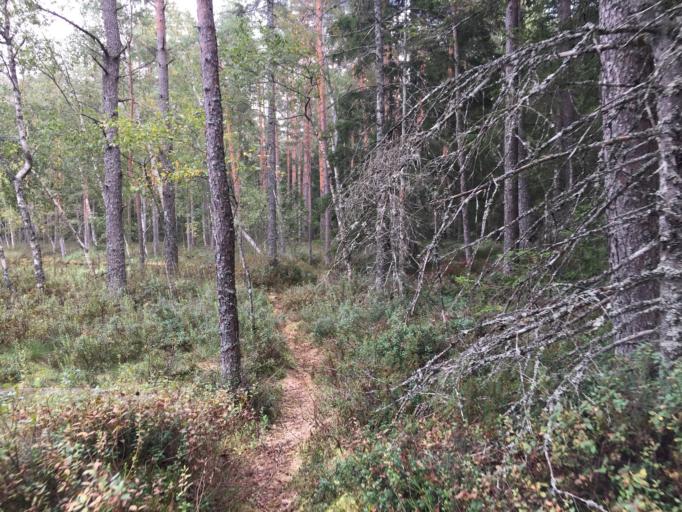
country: LV
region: Baldone
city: Baldone
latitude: 56.7830
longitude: 24.4444
